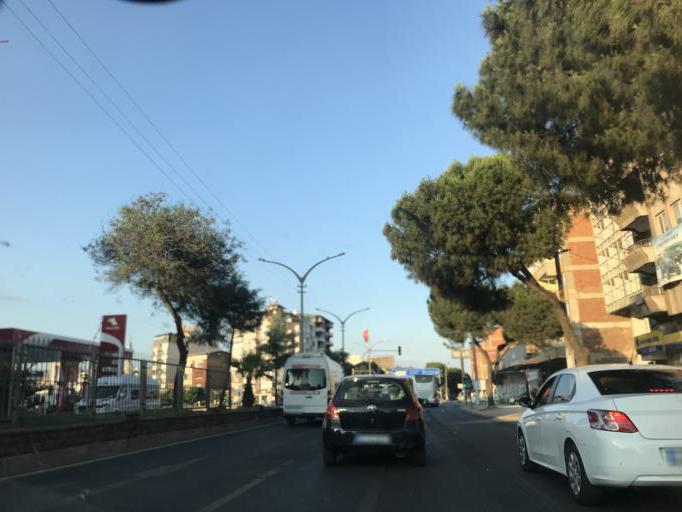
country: TR
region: Aydin
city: Nazilli
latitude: 37.9093
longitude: 28.3201
